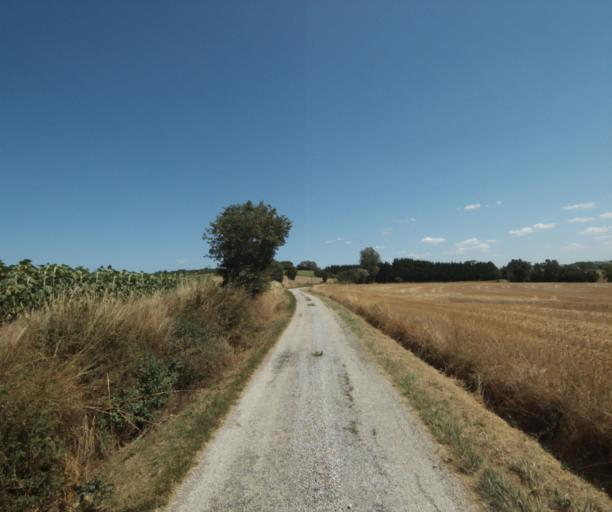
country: FR
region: Midi-Pyrenees
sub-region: Departement de la Haute-Garonne
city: Saint-Felix-Lauragais
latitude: 43.4945
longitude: 1.8816
